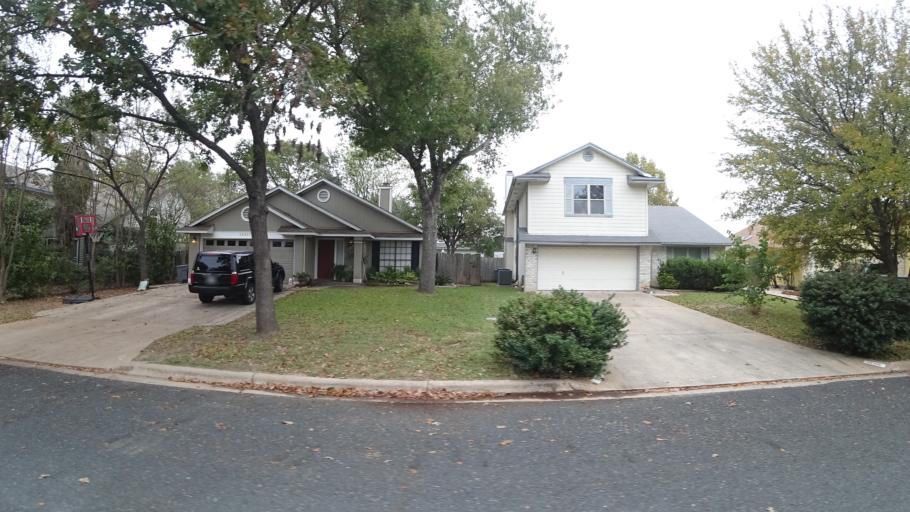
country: US
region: Texas
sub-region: Travis County
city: Wells Branch
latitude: 30.3917
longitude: -97.6556
